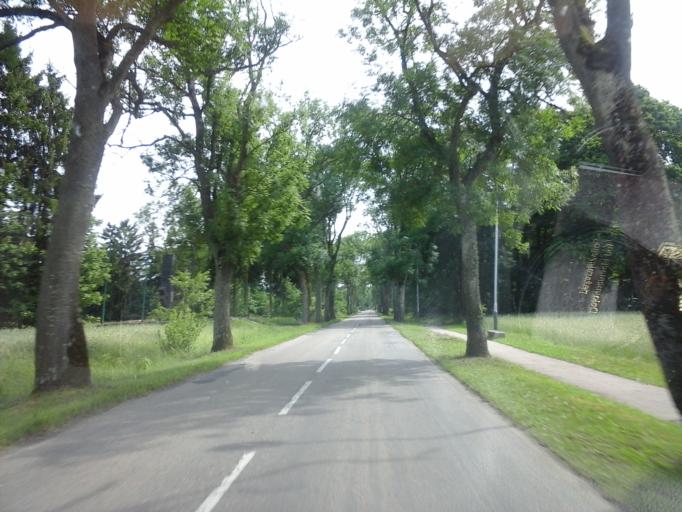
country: PL
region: West Pomeranian Voivodeship
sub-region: Powiat lobeski
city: Lobez
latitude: 53.6199
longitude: 15.6120
